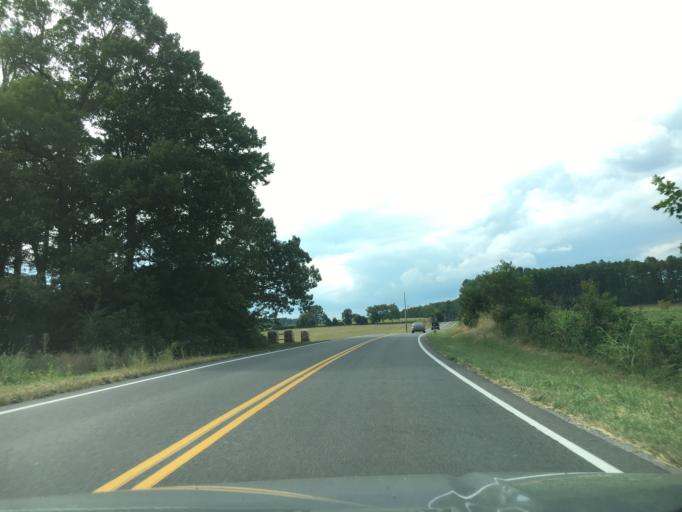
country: US
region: Virginia
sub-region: Campbell County
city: Rustburg
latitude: 37.2663
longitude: -79.1488
